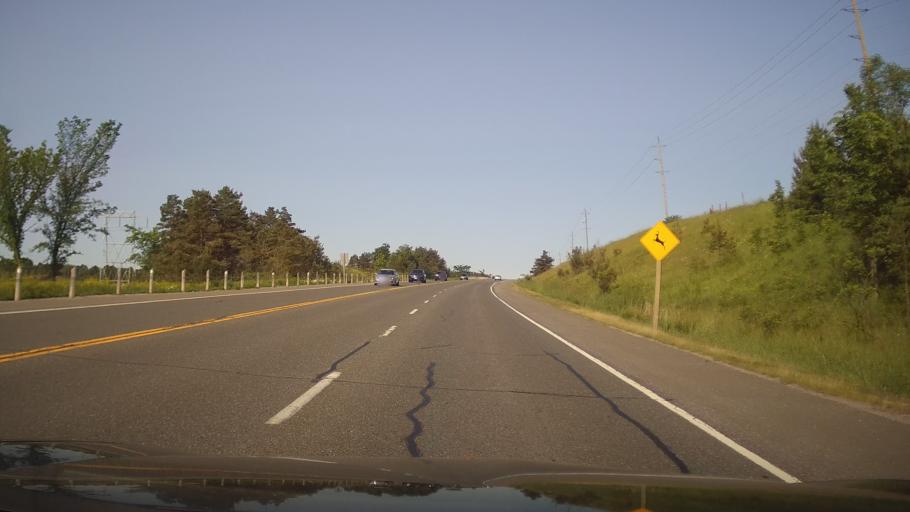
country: CA
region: Ontario
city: Peterborough
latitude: 44.3412
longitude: -78.0922
